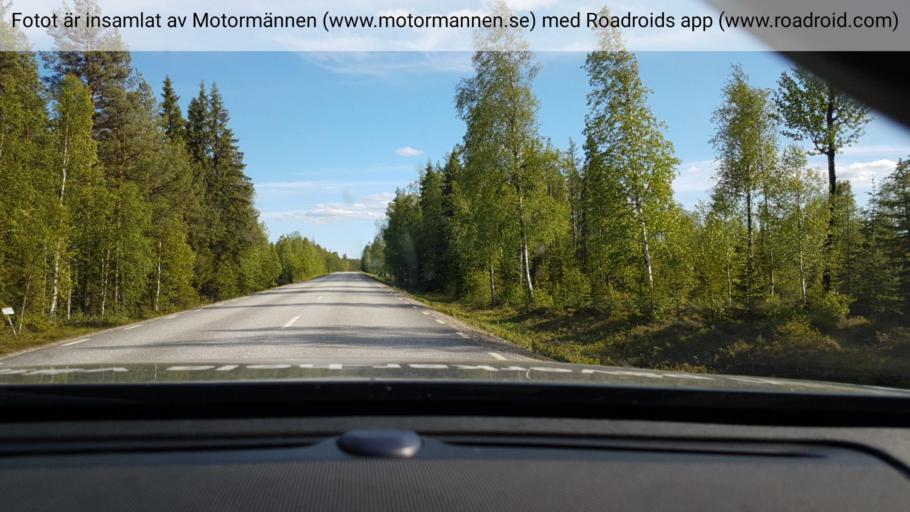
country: SE
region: Vaesterbotten
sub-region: Vindelns Kommun
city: Vindeln
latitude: 64.4019
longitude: 19.3725
